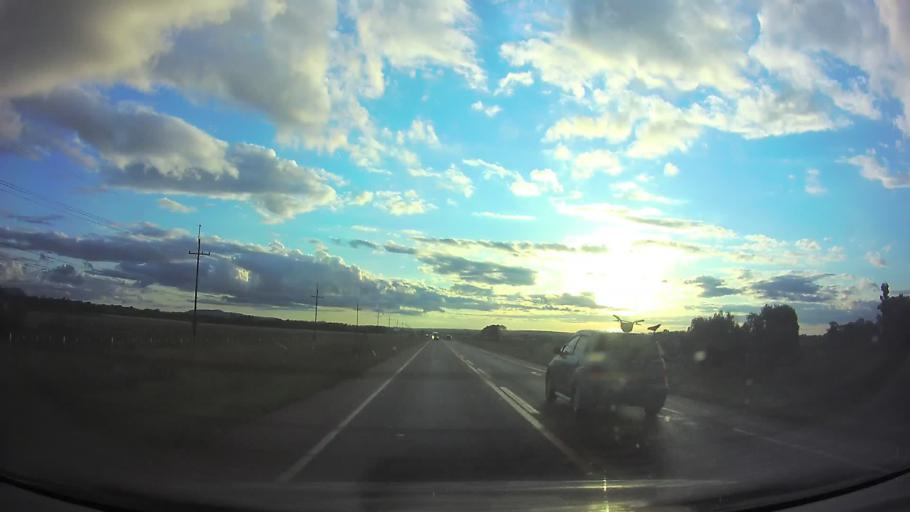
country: PY
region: Paraguari
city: Paraguari
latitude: -25.7104
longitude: -57.1892
